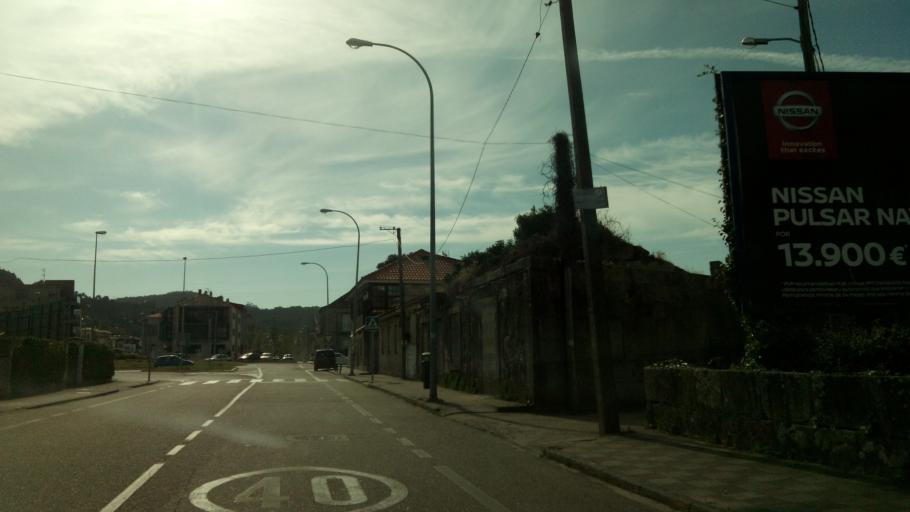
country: ES
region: Galicia
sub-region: Provincia de Pontevedra
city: Baiona
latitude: 42.1101
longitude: -8.8246
